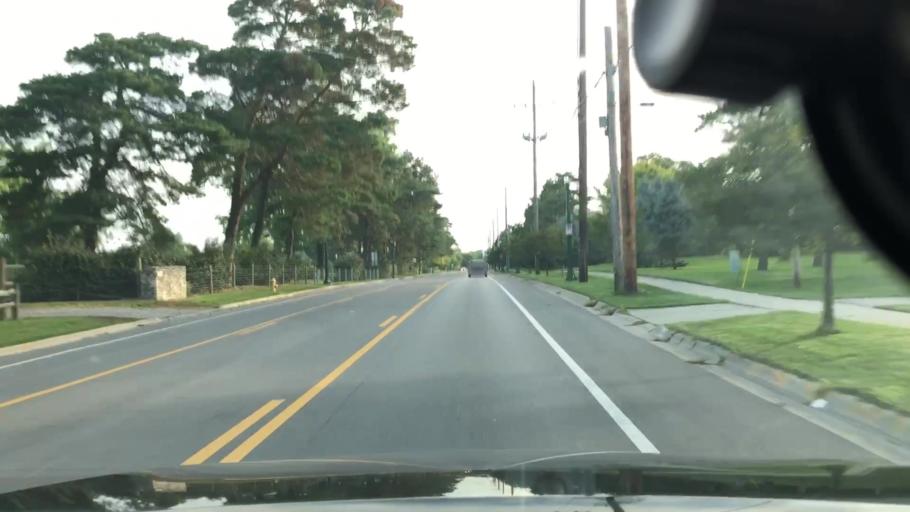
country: US
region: Ohio
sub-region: Franklin County
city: Upper Arlington
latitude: 40.0287
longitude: -83.0545
